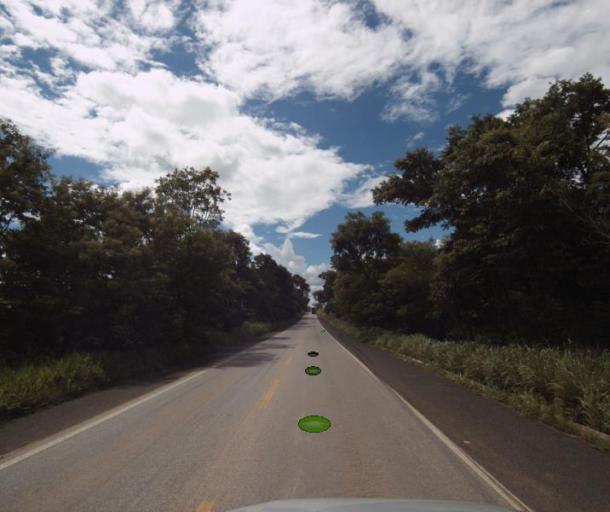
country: BR
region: Goias
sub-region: Porangatu
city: Porangatu
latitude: -13.8806
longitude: -49.0546
